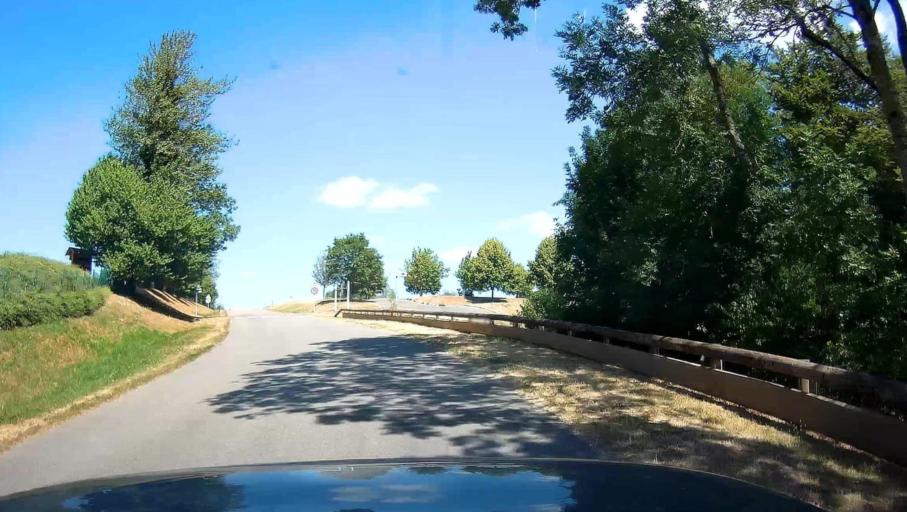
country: FR
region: Champagne-Ardenne
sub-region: Departement de la Haute-Marne
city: Langres
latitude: 47.8717
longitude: 5.3812
